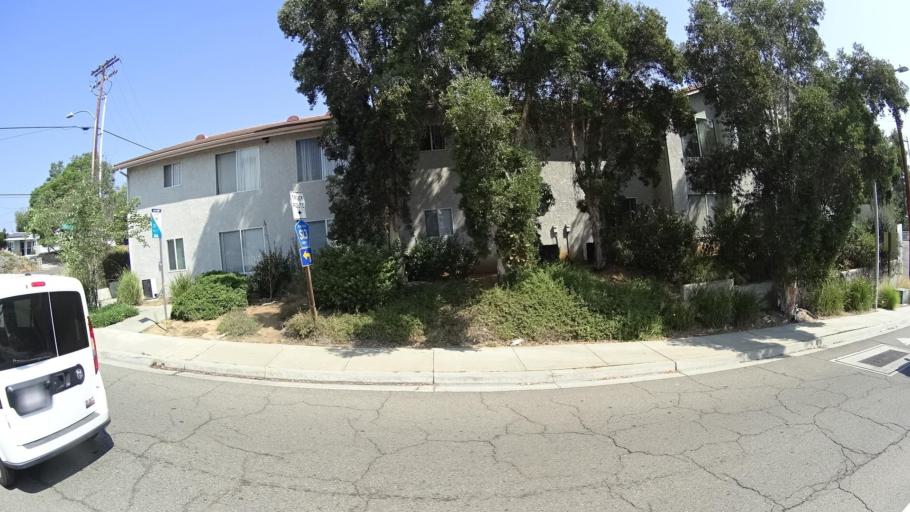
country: US
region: California
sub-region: San Diego County
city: Fallbrook
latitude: 33.3847
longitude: -117.2532
